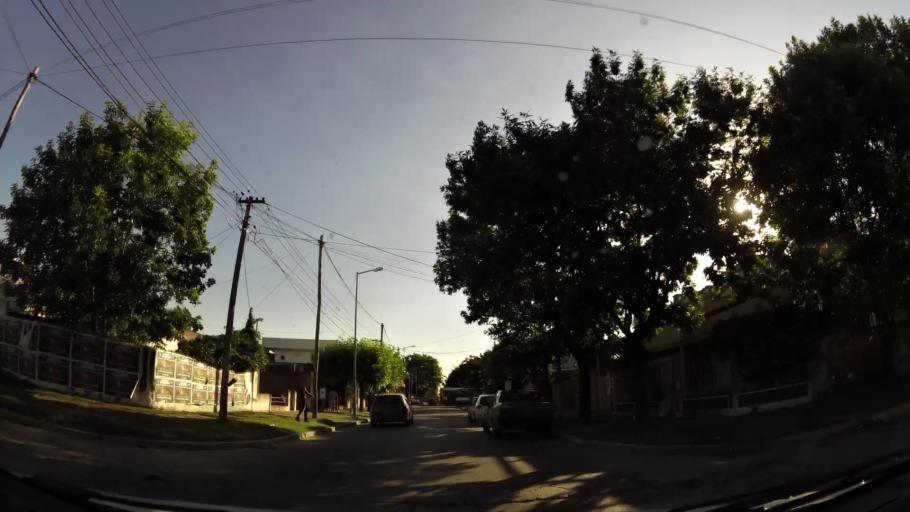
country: AR
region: Buenos Aires
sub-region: Partido de Merlo
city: Merlo
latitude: -34.6841
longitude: -58.7319
